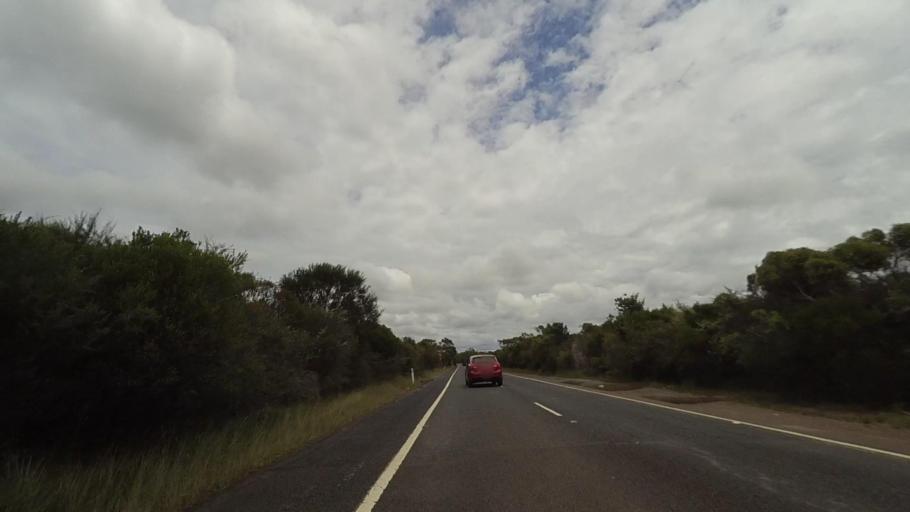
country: AU
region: New South Wales
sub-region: Sutherland Shire
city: Grays Point
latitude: -34.0878
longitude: 151.0674
